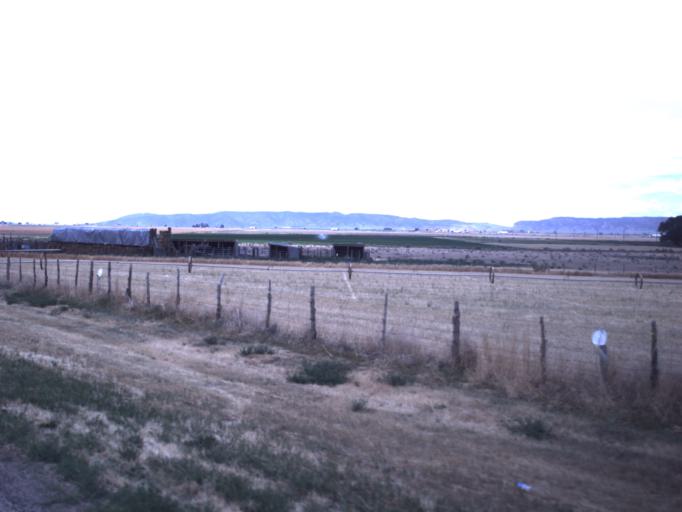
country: US
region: Utah
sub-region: Iron County
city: Parowan
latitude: 37.8729
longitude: -112.7908
